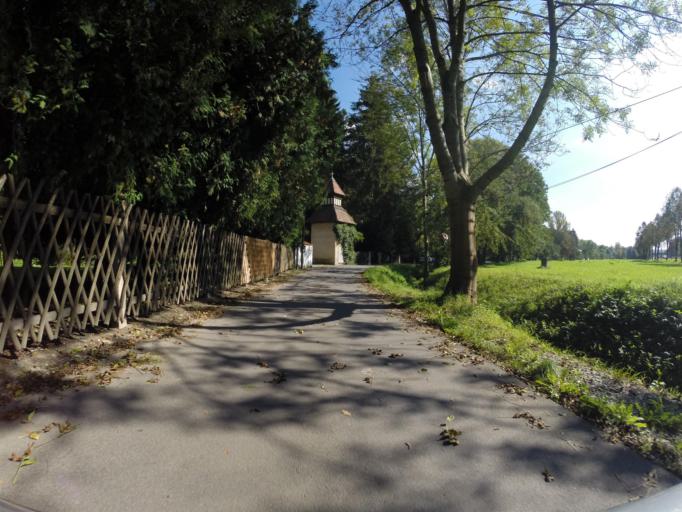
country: DE
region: Thuringia
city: Jena
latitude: 50.9022
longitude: 11.5989
